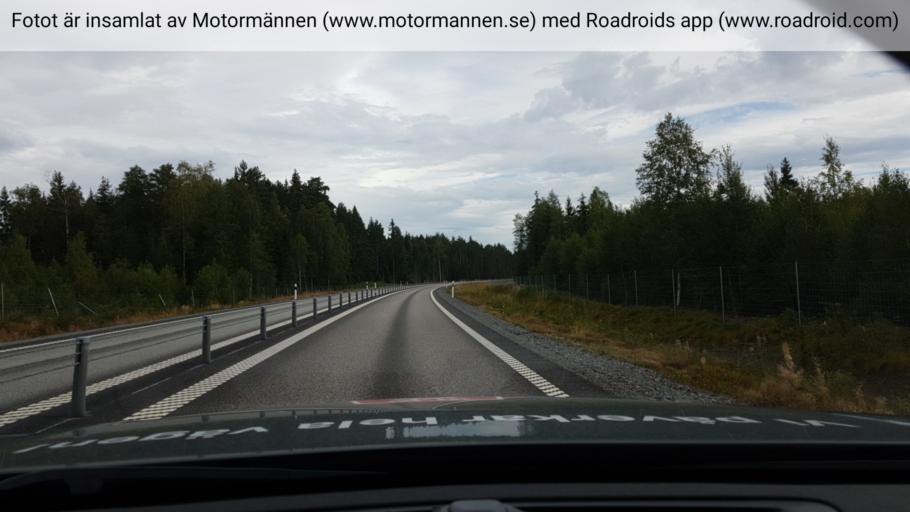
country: SE
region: Uppsala
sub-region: Heby Kommun
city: Heby
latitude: 60.0410
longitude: 16.8731
